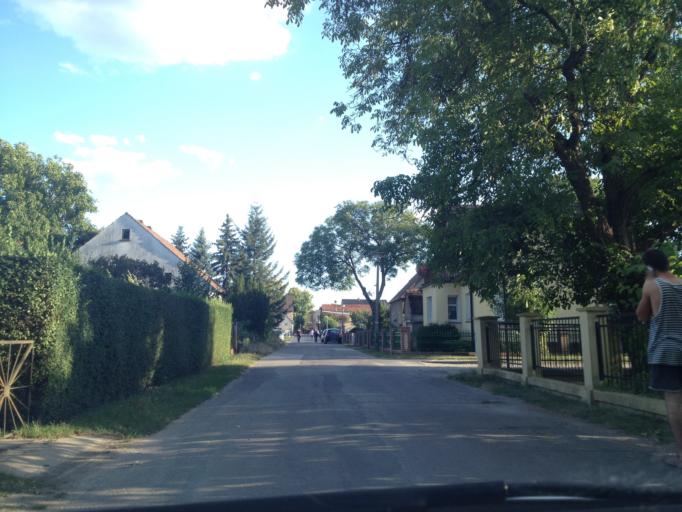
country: DE
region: Brandenburg
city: Vetschau
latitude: 51.7875
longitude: 14.0764
